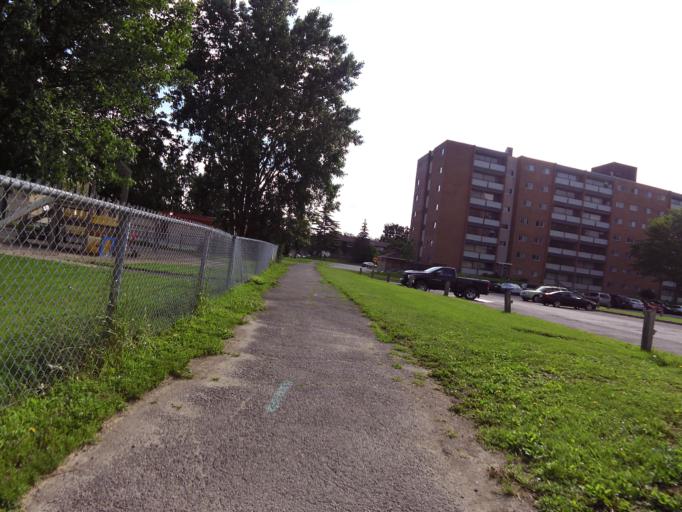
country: CA
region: Ontario
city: Bells Corners
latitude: 45.3500
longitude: -75.8075
